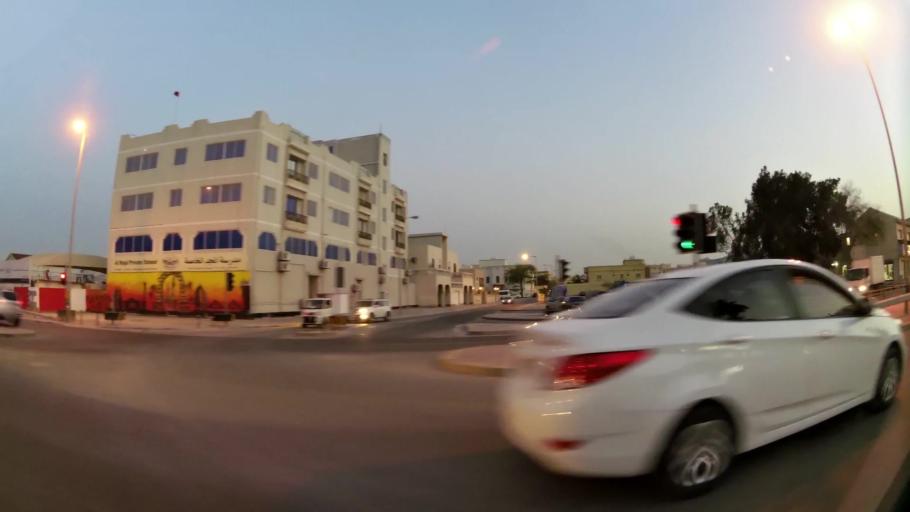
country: BH
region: Manama
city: Jidd Hafs
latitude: 26.2131
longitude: 50.5569
